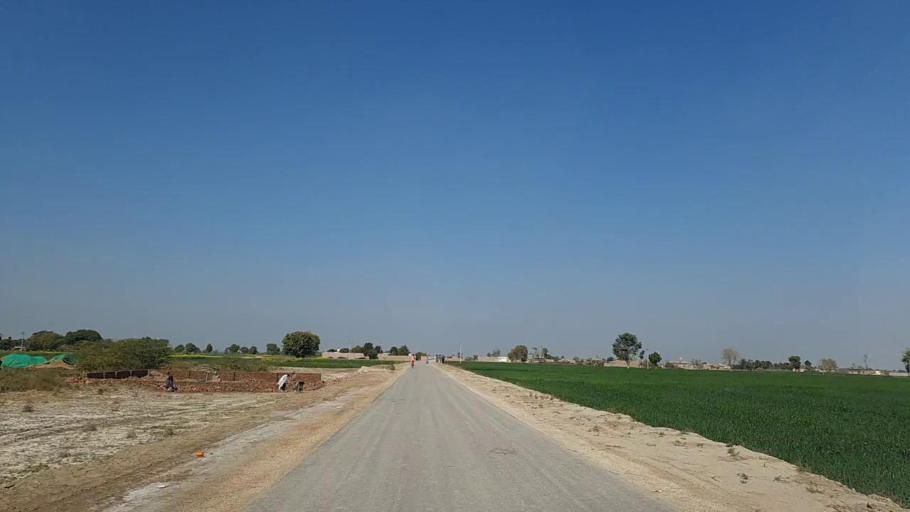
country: PK
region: Sindh
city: Nawabshah
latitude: 26.2462
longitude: 68.4512
